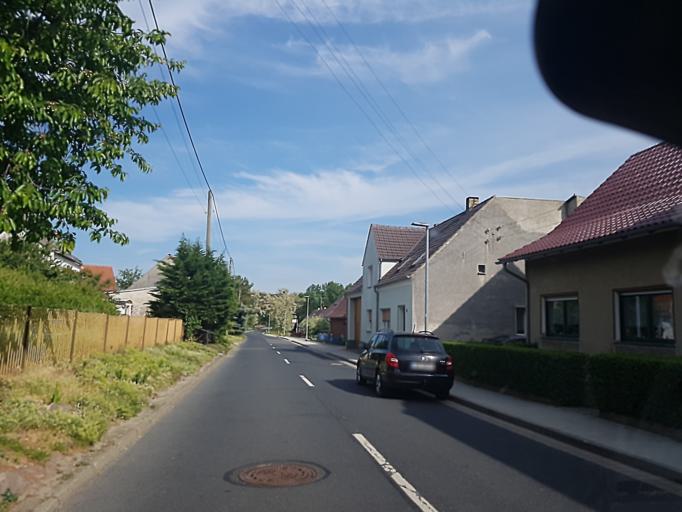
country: DE
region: Saxony-Anhalt
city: Kropstadt
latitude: 51.9880
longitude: 12.6886
